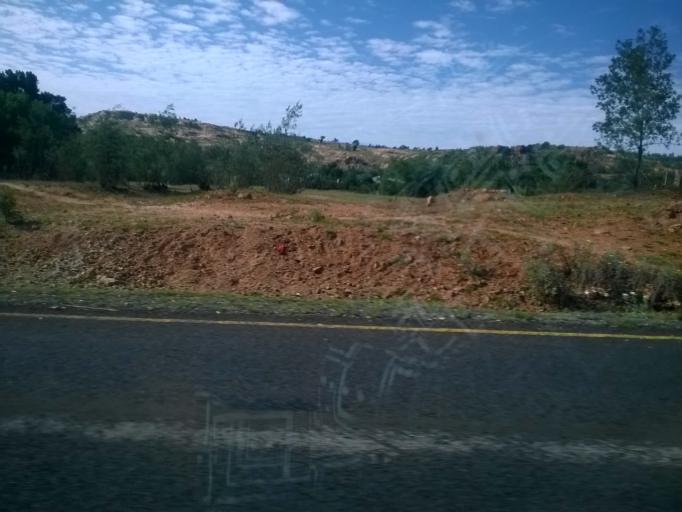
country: LS
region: Berea
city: Teyateyaneng
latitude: -29.1078
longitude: 27.8286
